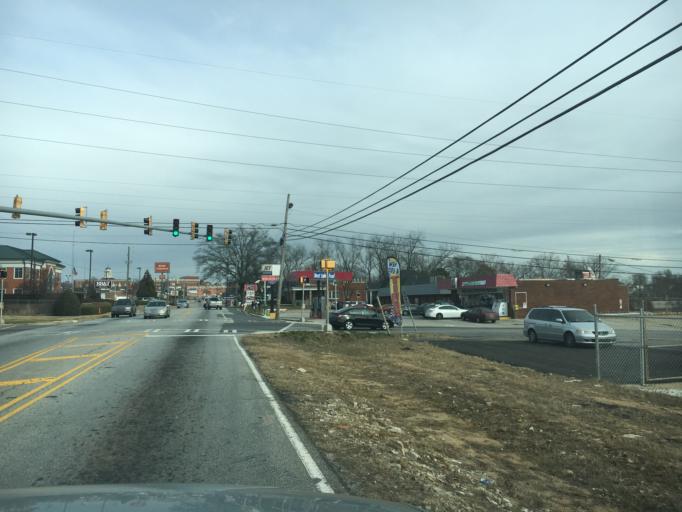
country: US
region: Georgia
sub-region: Barrow County
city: Winder
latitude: 33.9891
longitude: -83.7269
